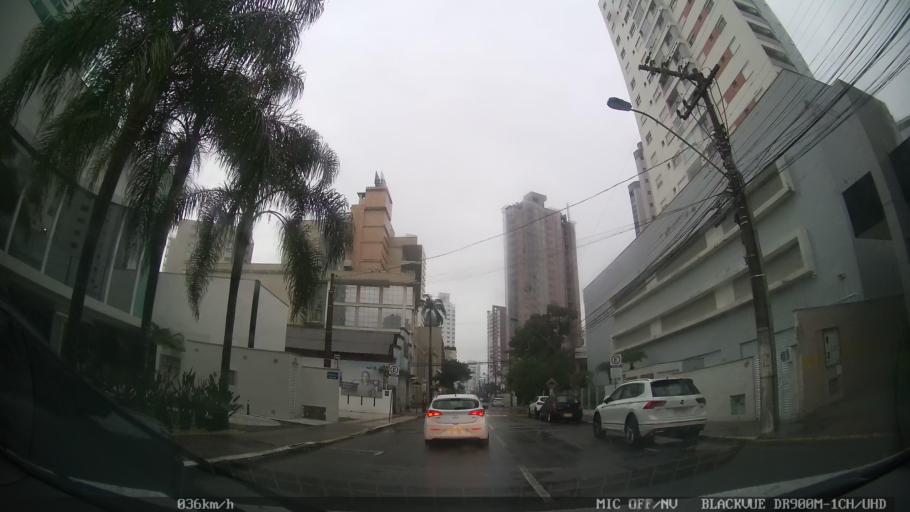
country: BR
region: Santa Catarina
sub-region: Itajai
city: Itajai
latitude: -26.9090
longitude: -48.6570
